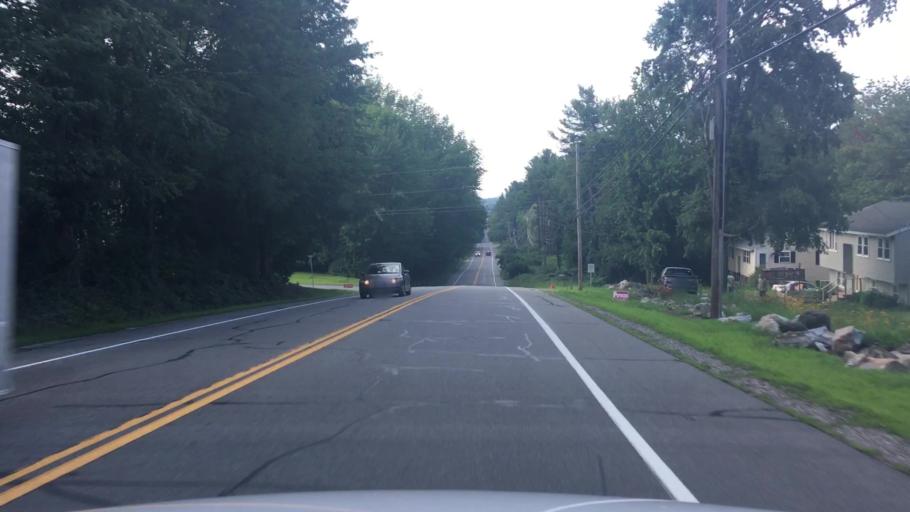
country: US
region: New Hampshire
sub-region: Rockingham County
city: Derry Village
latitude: 42.9296
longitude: -71.3389
